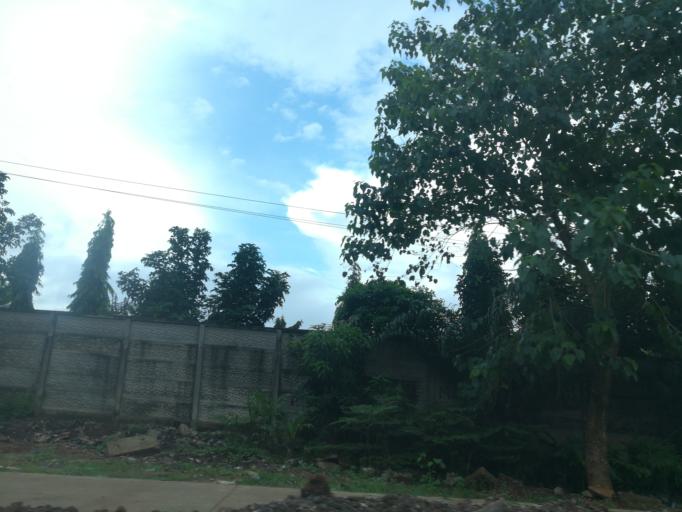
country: NG
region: Lagos
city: Ikeja
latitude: 6.5861
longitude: 3.3393
